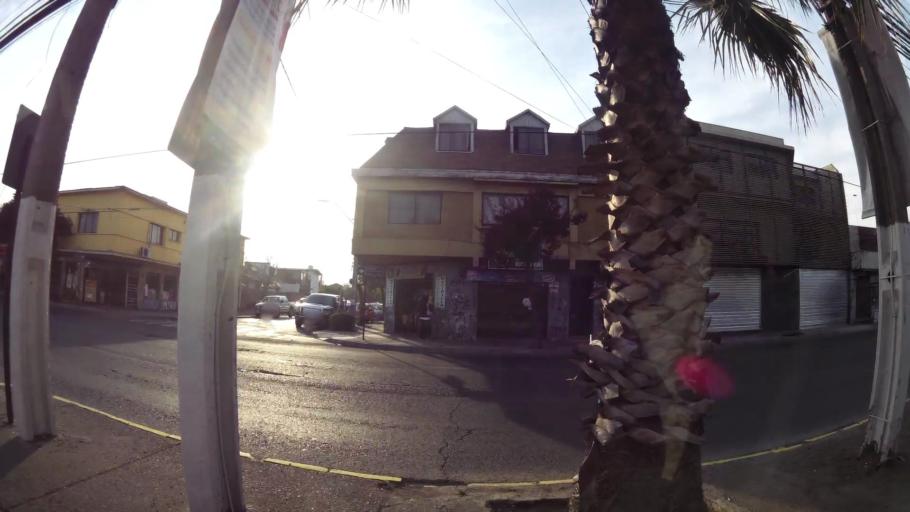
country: CL
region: Santiago Metropolitan
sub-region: Provincia de Santiago
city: La Pintana
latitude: -33.5329
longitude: -70.6632
